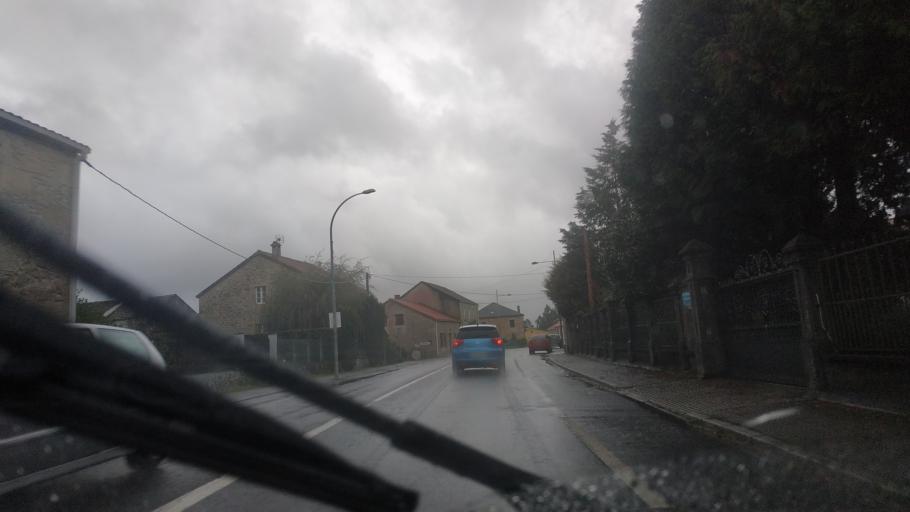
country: ES
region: Galicia
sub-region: Provincia da Coruna
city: Negreira
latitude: 42.9236
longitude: -8.7341
